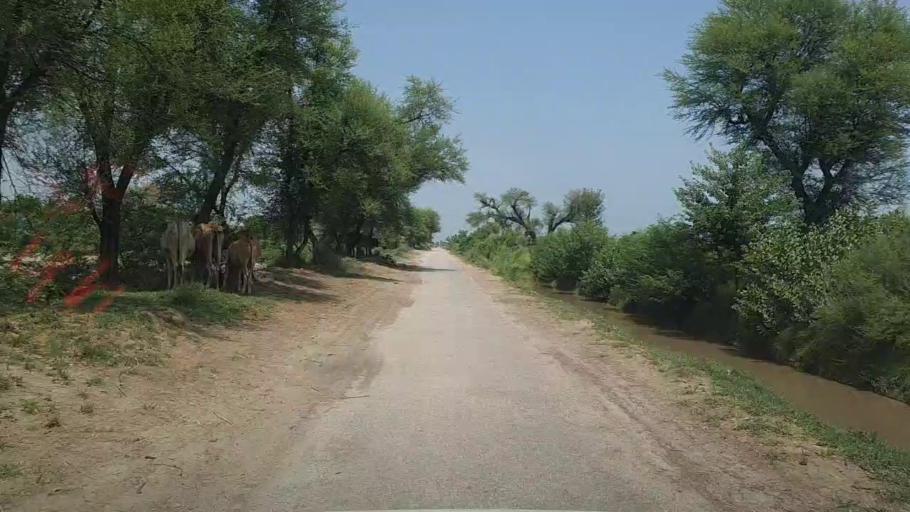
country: PK
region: Sindh
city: Karaundi
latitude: 26.8752
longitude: 68.3362
